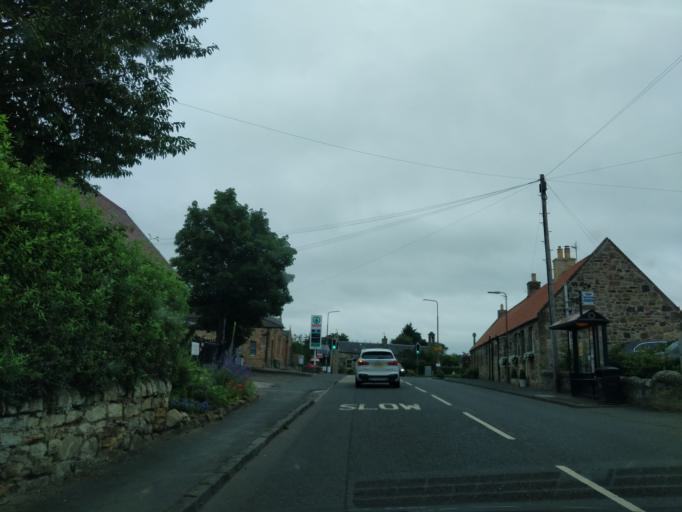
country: GB
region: Scotland
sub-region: East Lothian
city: Pencaitland
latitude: 55.9099
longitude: -2.8970
